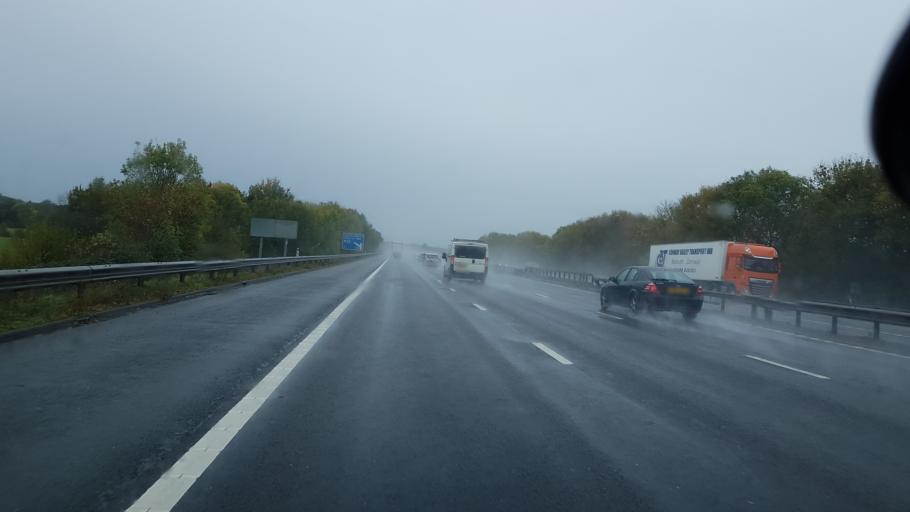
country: GB
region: England
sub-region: Worcestershire
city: Bredon
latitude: 52.0273
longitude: -2.1235
